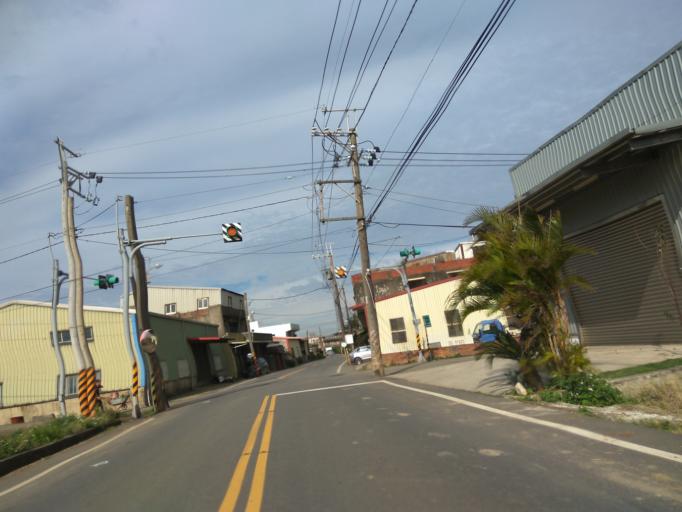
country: TW
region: Taiwan
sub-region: Hsinchu
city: Zhubei
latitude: 24.9533
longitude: 121.1277
